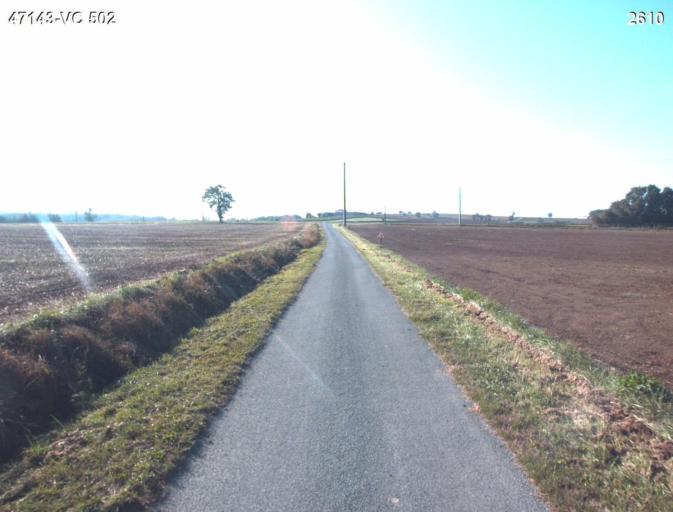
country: FR
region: Aquitaine
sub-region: Departement du Lot-et-Garonne
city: Vianne
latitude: 44.1860
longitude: 0.3306
